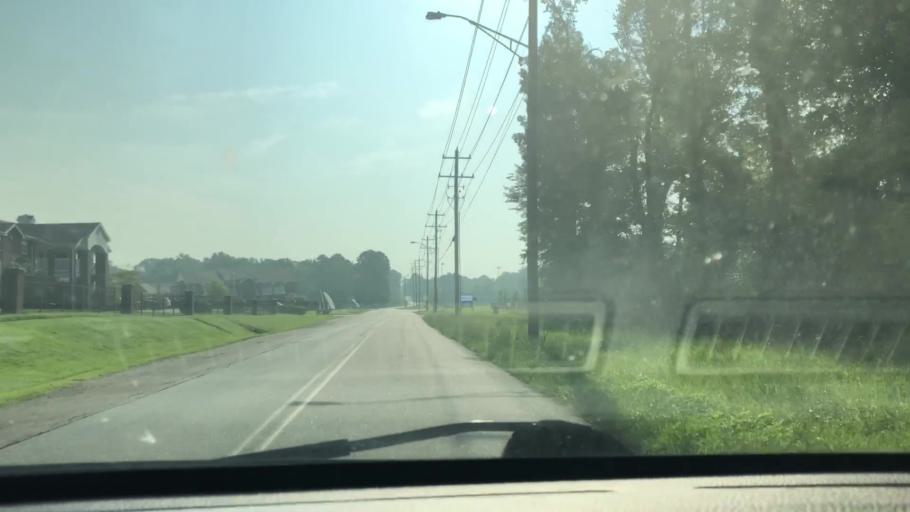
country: US
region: Arkansas
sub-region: Saline County
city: Bryant
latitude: 34.5957
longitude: -92.5168
